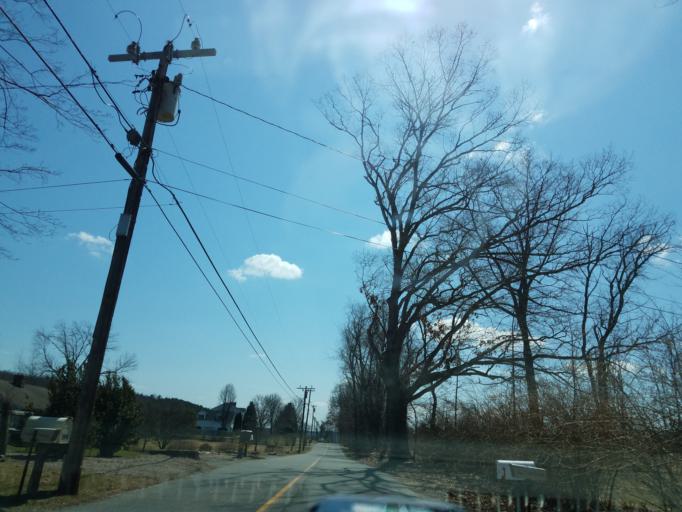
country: US
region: Connecticut
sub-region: Litchfield County
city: Bethlehem Village
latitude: 41.6187
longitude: -73.1712
